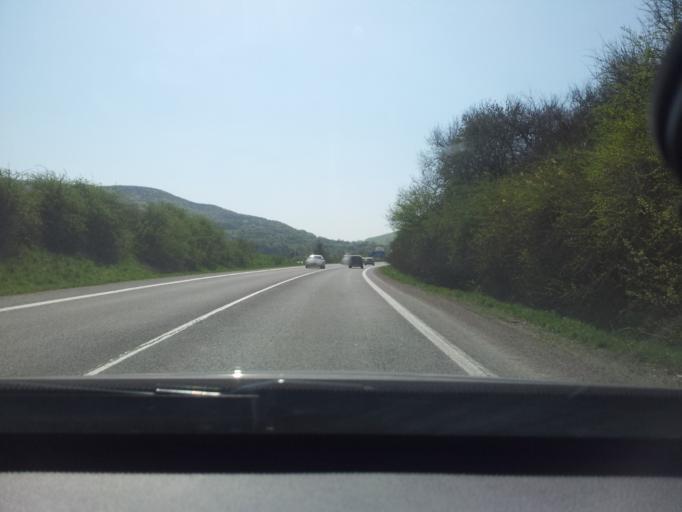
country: SK
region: Trenciansky
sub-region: Okres Trencin
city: Trencin
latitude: 48.8417
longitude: 18.0546
